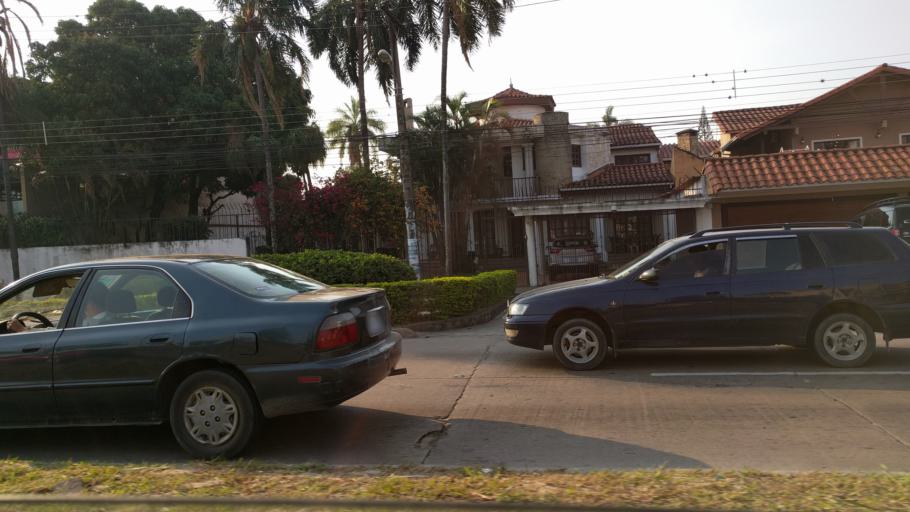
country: BO
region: Santa Cruz
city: Santa Cruz de la Sierra
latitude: -17.7974
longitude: -63.1671
